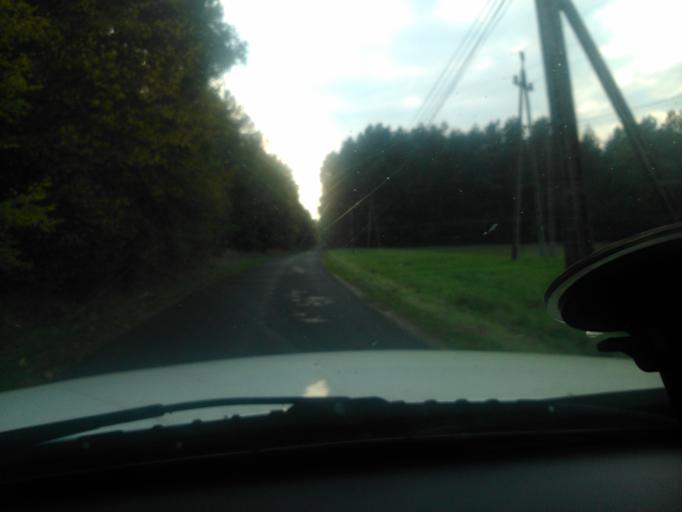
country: PL
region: Kujawsko-Pomorskie
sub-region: Powiat golubsko-dobrzynski
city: Radomin
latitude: 53.1470
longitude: 19.1329
